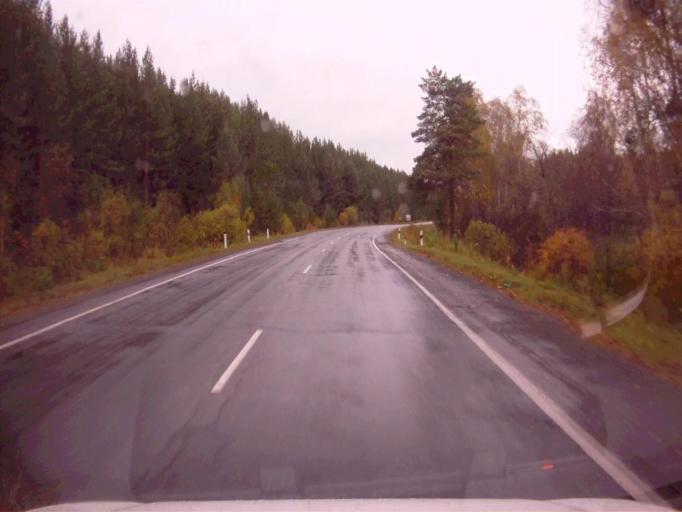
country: RU
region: Chelyabinsk
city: Verkhniy Ufaley
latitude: 56.0128
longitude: 60.3149
